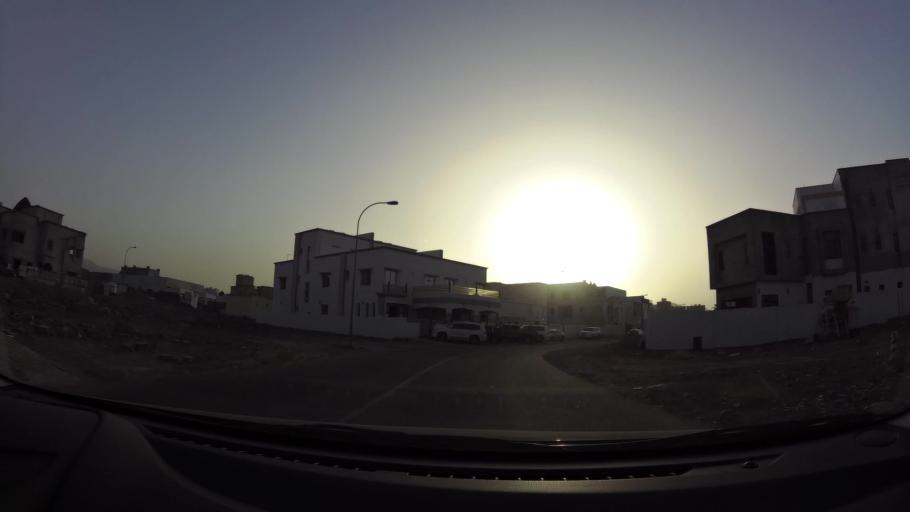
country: OM
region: Muhafazat Masqat
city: Bawshar
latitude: 23.4997
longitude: 58.3354
